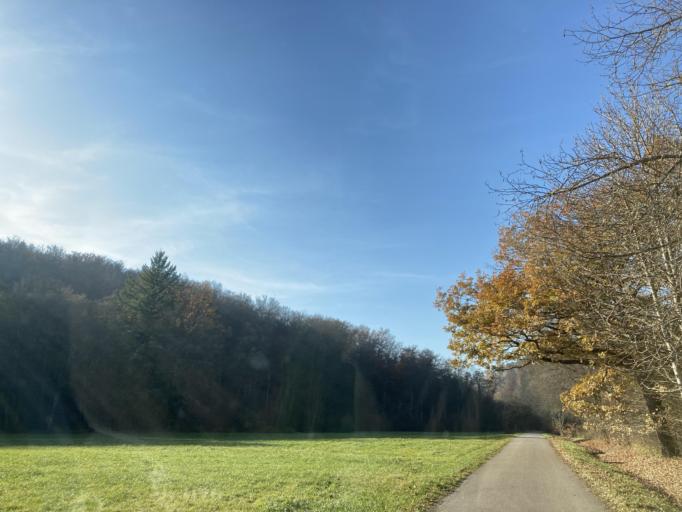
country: DE
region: Baden-Wuerttemberg
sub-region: Tuebingen Region
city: Tuebingen
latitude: 48.5582
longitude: 9.0476
